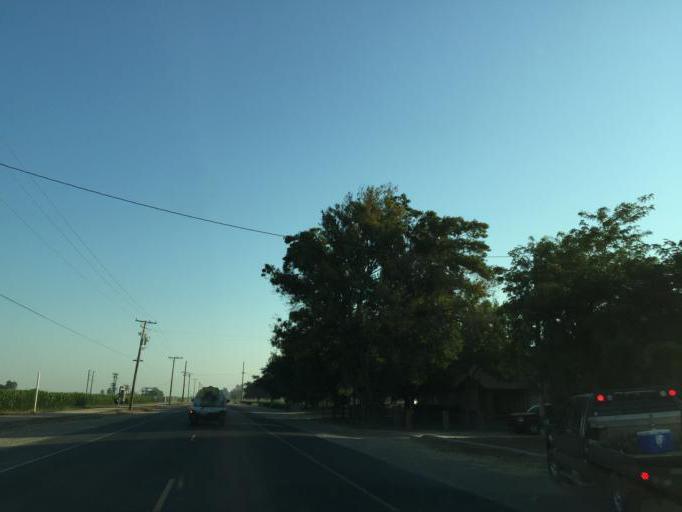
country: US
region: California
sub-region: Tulare County
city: Visalia
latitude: 36.4118
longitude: -119.2961
